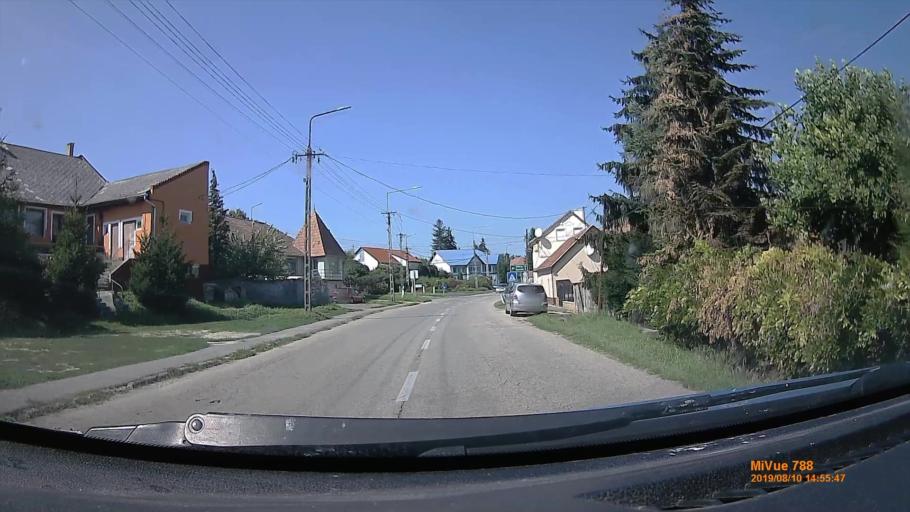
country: HU
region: Somogy
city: Lengyeltoti
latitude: 46.6636
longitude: 17.6353
